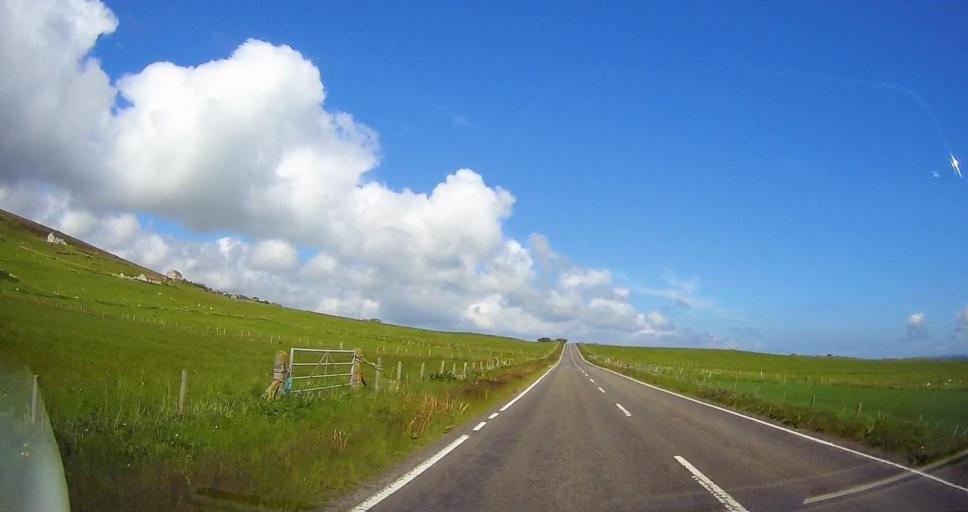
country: GB
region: Scotland
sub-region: Orkney Islands
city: Orkney
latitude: 59.0160
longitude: -3.1063
